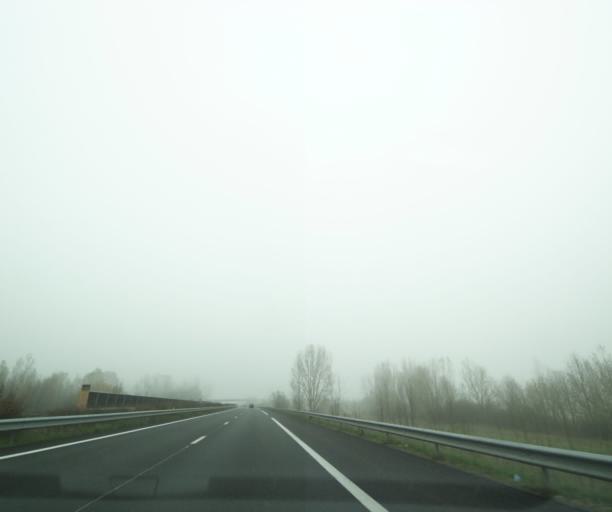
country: FR
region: Midi-Pyrenees
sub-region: Departement du Tarn-et-Garonne
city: Realville
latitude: 44.1146
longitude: 1.4707
